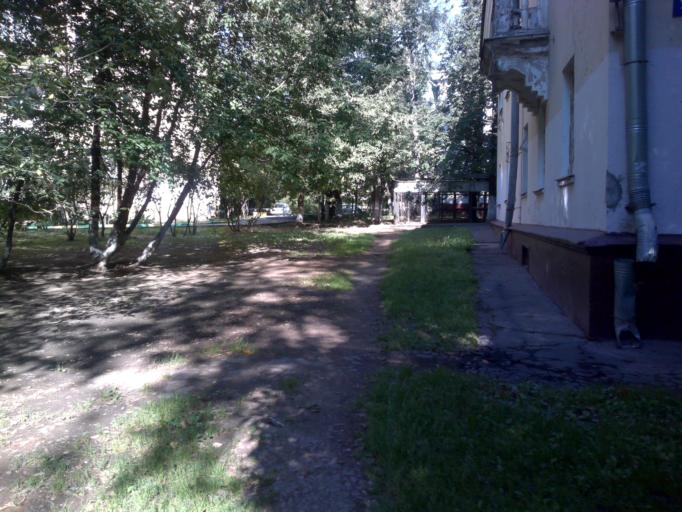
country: RU
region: Moskovskaya
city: Leninskiye Gory
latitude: 55.6943
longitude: 37.5686
